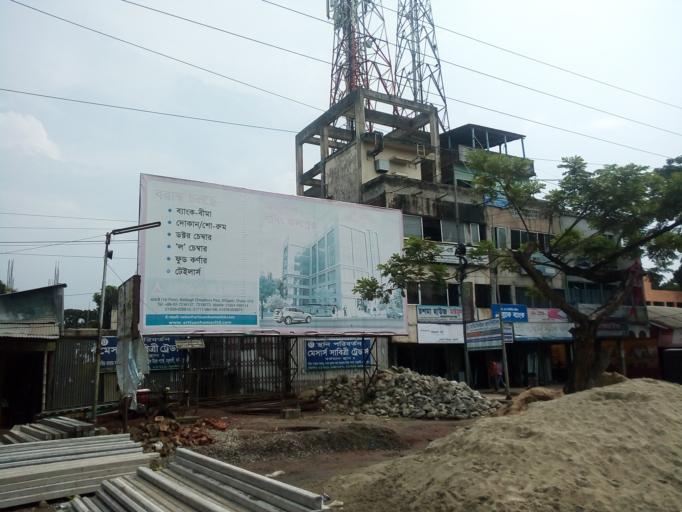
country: BD
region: Khulna
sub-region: Magura
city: Magura
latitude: 23.5430
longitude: 89.6273
